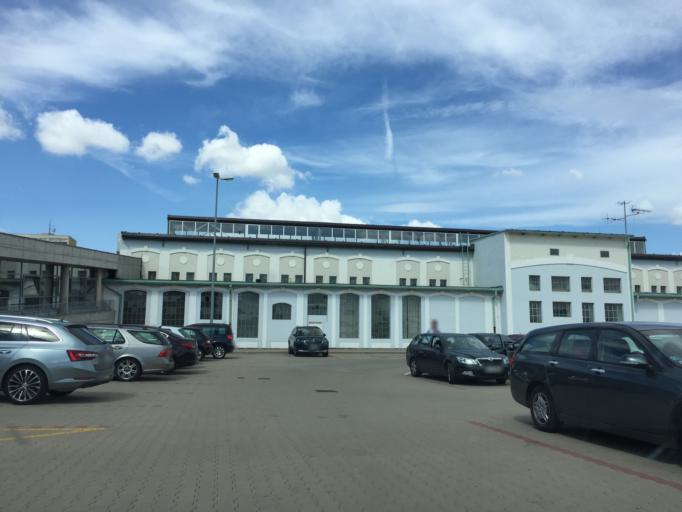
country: CZ
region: Central Bohemia
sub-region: Okres Mlada Boleslav
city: Mlada Boleslav
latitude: 50.4182
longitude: 14.9165
